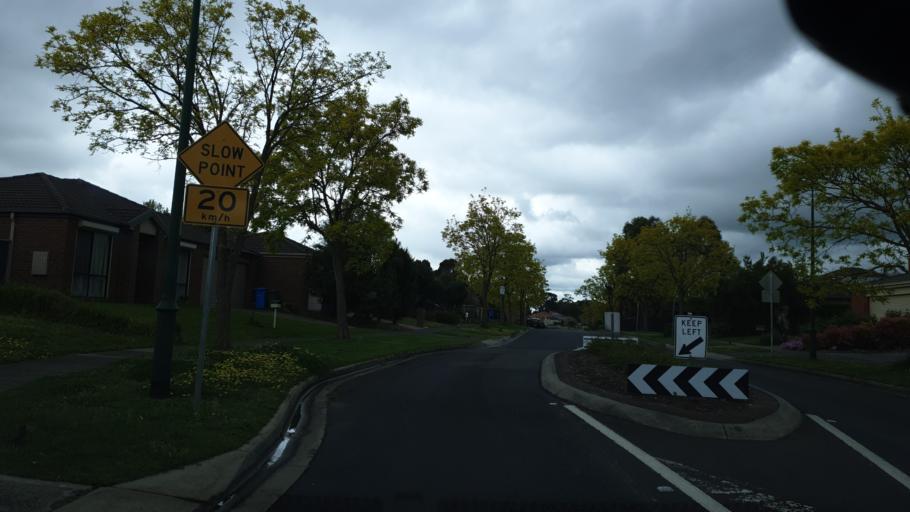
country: AU
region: Victoria
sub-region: Casey
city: Cranbourne North
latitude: -38.0637
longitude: 145.2850
